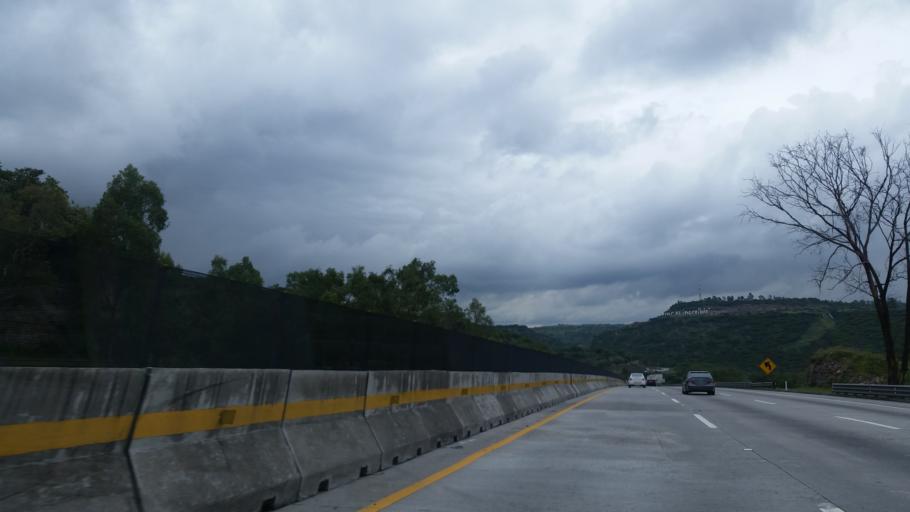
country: MX
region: Hidalgo
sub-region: Tepeji del Rio de Ocampo
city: Santiago Tlautla
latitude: 19.9524
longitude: -99.4056
